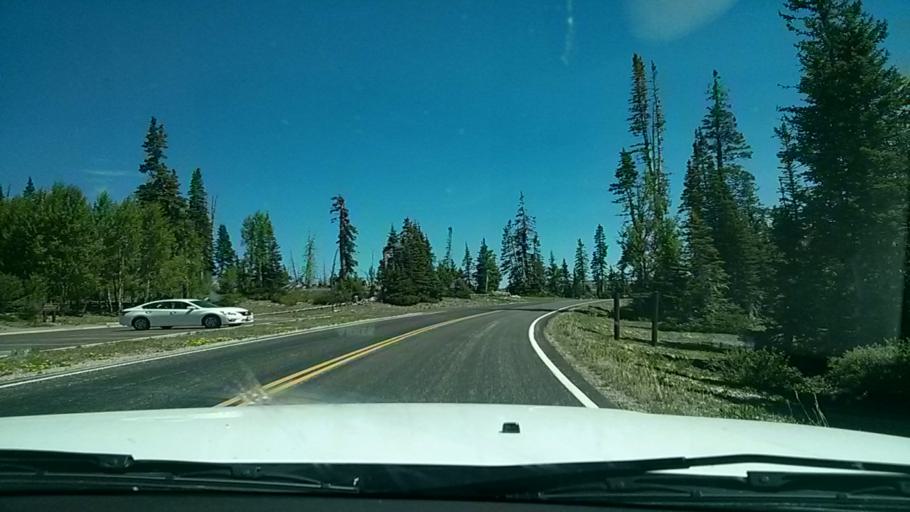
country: US
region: Utah
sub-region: Iron County
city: Parowan
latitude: 37.6413
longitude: -112.8219
